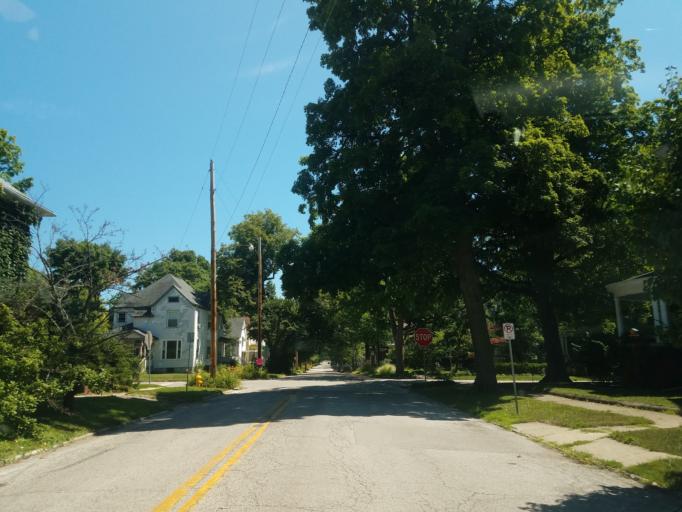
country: US
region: Illinois
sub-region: McLean County
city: Bloomington
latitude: 40.4783
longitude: -88.9885
